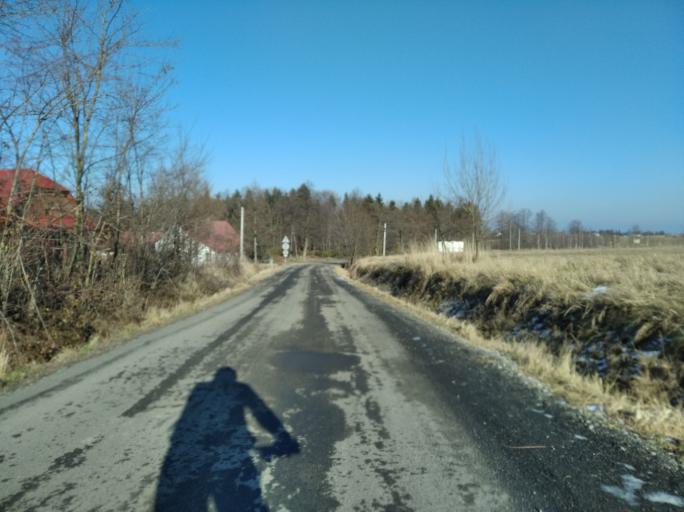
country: PL
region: Subcarpathian Voivodeship
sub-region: Powiat rzeszowski
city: Straszydle
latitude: 49.8761
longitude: 21.9808
